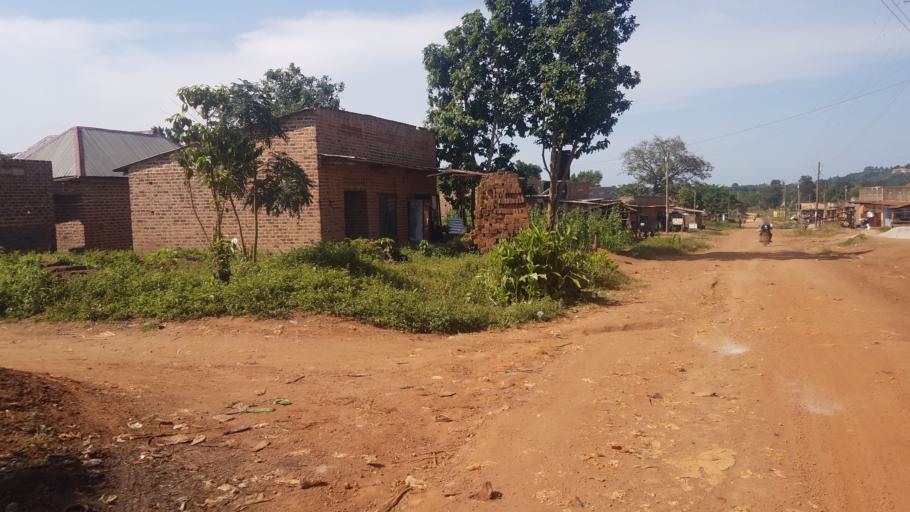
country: UG
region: Central Region
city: Masaka
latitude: -0.3114
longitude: 31.6817
